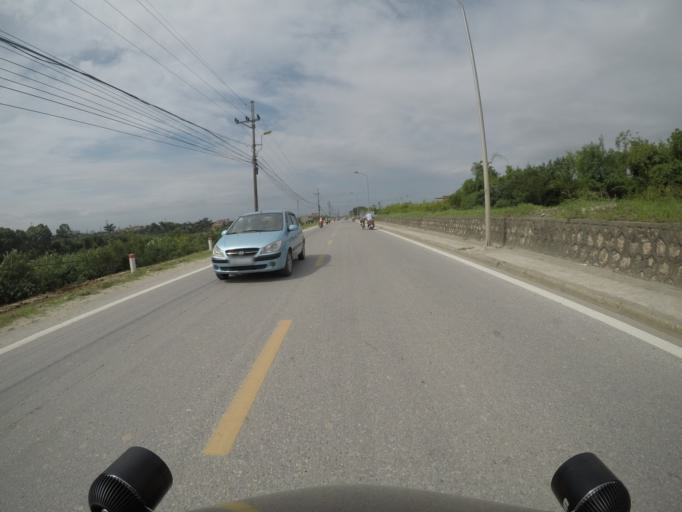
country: VN
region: Ha Noi
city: Cau Dien
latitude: 21.0897
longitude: 105.7627
